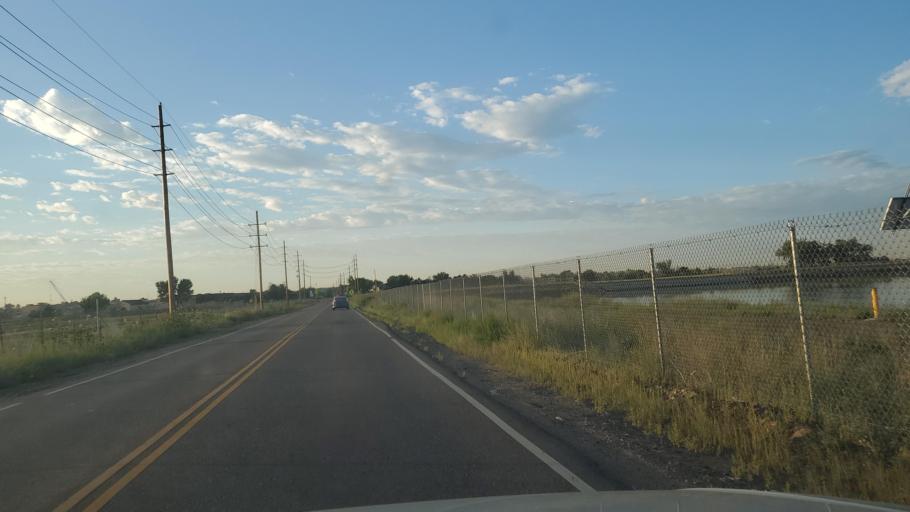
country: US
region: Colorado
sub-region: Adams County
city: Derby
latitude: 39.8767
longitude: -104.9150
